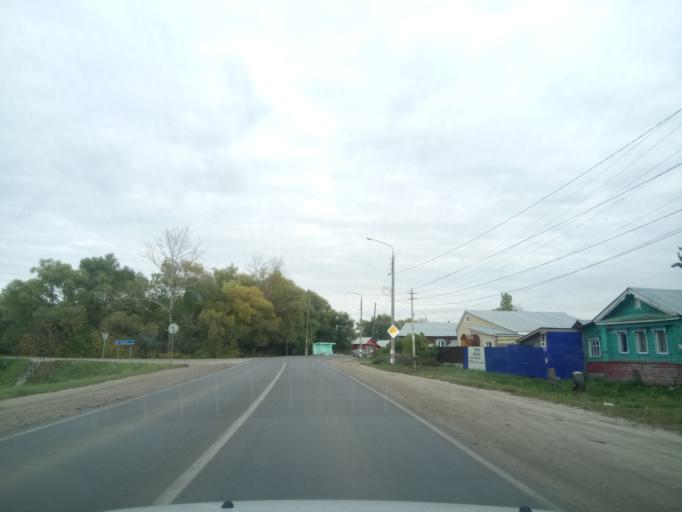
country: RU
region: Nizjnij Novgorod
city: Lukoyanov
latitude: 55.0312
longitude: 44.4808
